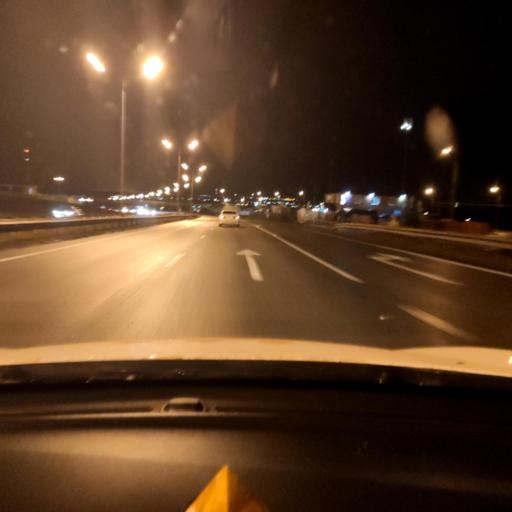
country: RU
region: Tatarstan
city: Osinovo
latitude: 55.7704
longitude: 48.8358
